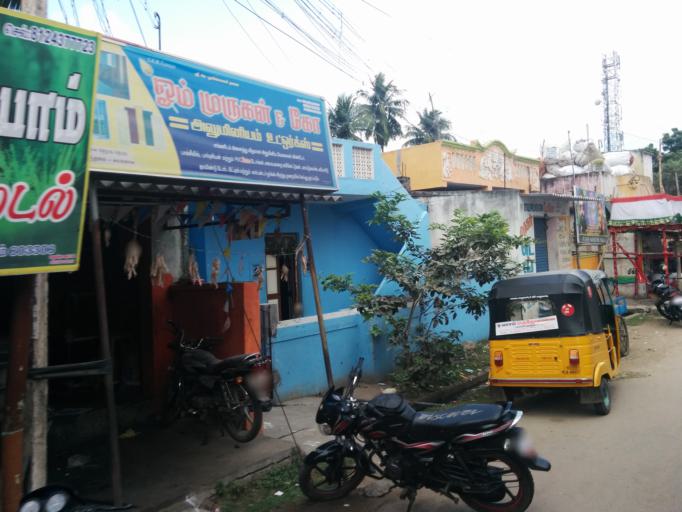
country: IN
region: Tamil Nadu
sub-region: Kancheepuram
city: Madurantakam
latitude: 12.5102
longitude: 79.8889
